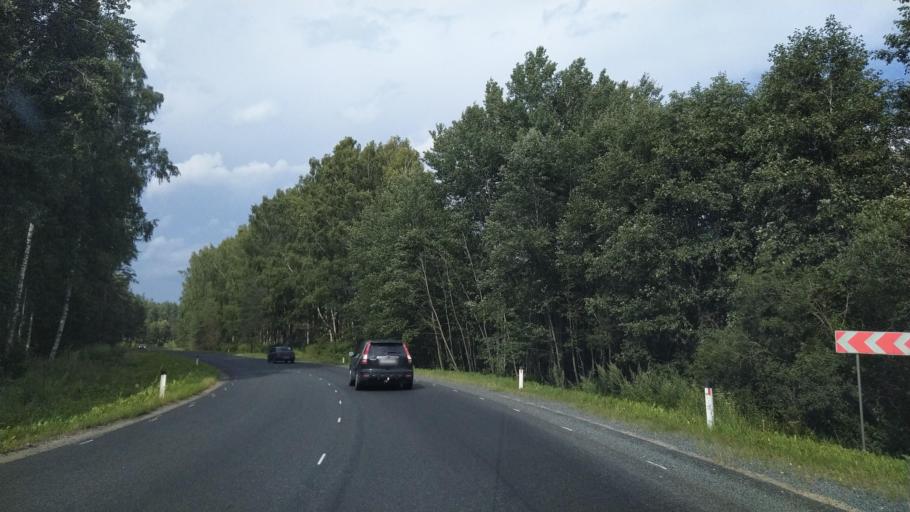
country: RU
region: Pskov
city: Porkhov
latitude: 57.8424
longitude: 29.5448
